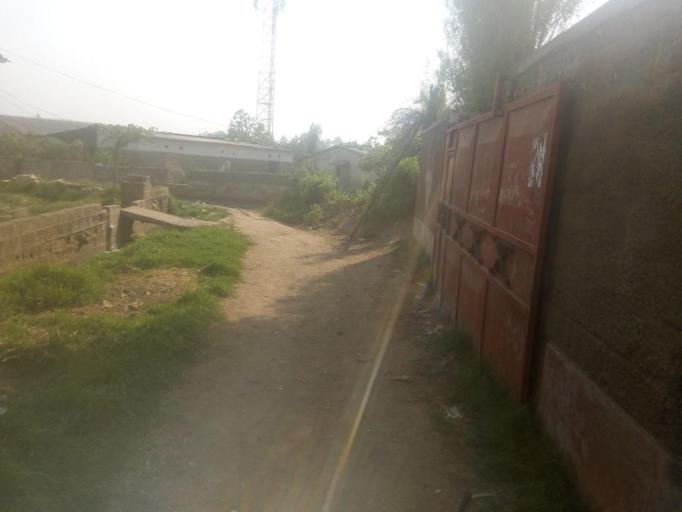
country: ZM
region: Lusaka
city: Lusaka
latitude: -15.4059
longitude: 28.3614
